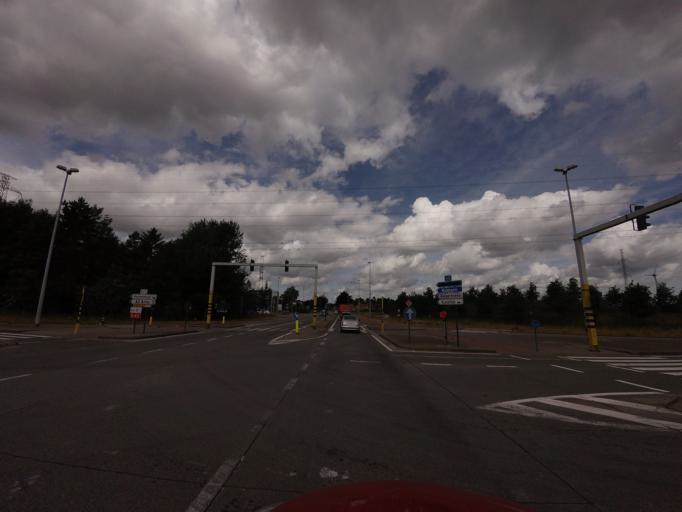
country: BE
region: Flanders
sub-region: Provincie Oost-Vlaanderen
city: Eeklo
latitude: 51.1981
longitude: 3.5336
